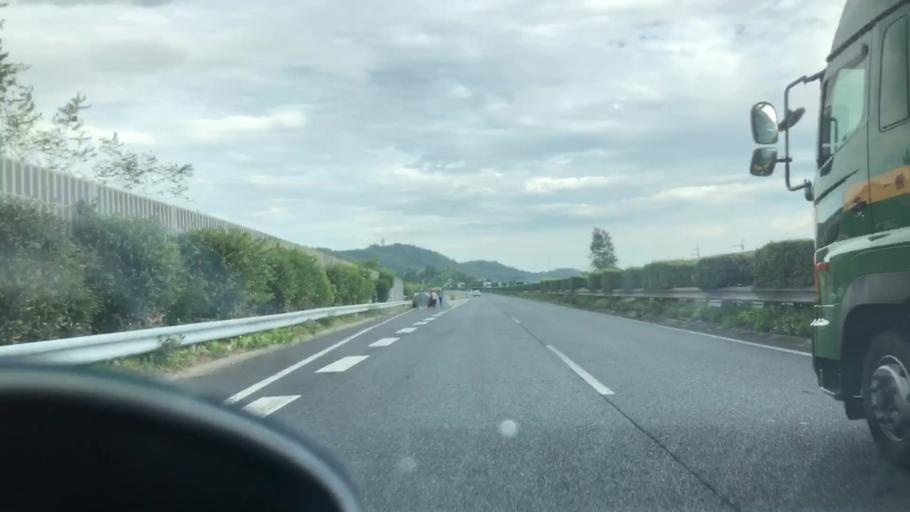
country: JP
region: Hyogo
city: Ono
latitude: 34.9365
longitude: 134.8343
